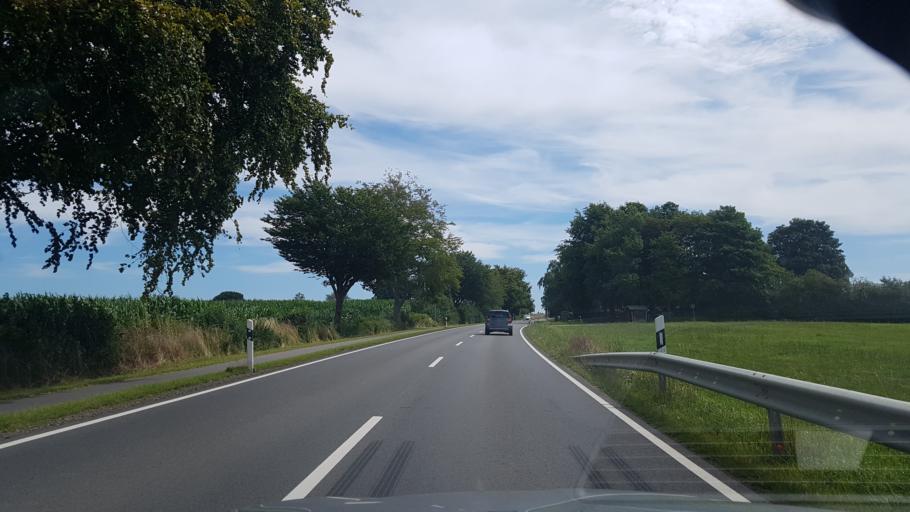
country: DE
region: Schleswig-Holstein
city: Warnau
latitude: 54.1694
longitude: 10.1529
